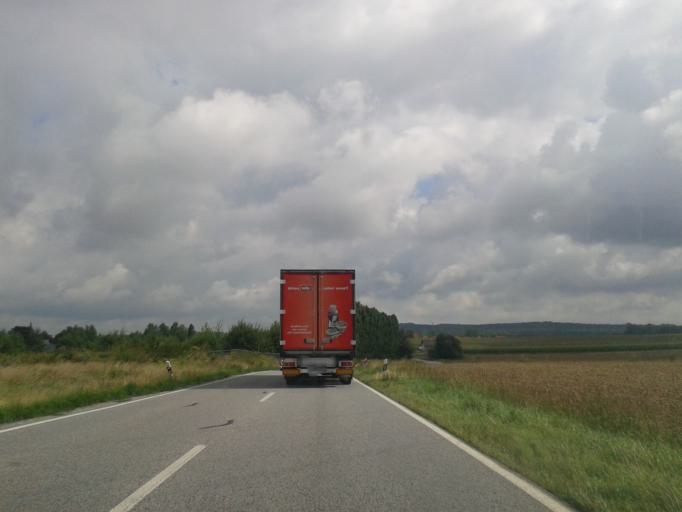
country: DE
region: Saxony
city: Lichtenberg
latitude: 51.1459
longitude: 13.9573
